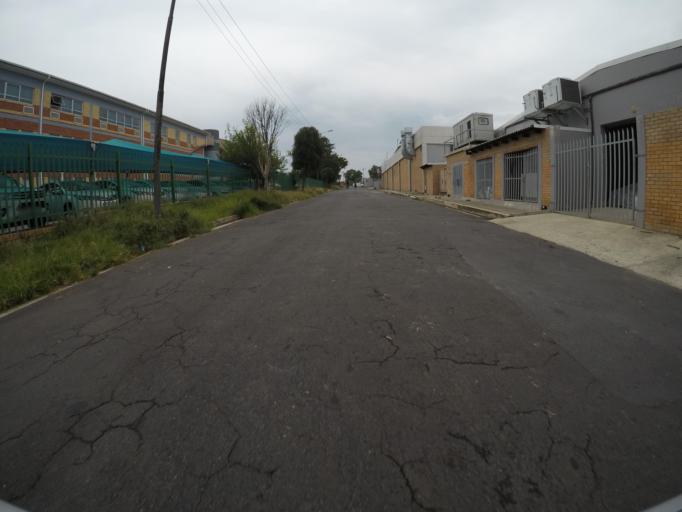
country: ZA
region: Eastern Cape
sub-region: Buffalo City Metropolitan Municipality
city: East London
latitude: -32.9807
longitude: 27.9003
